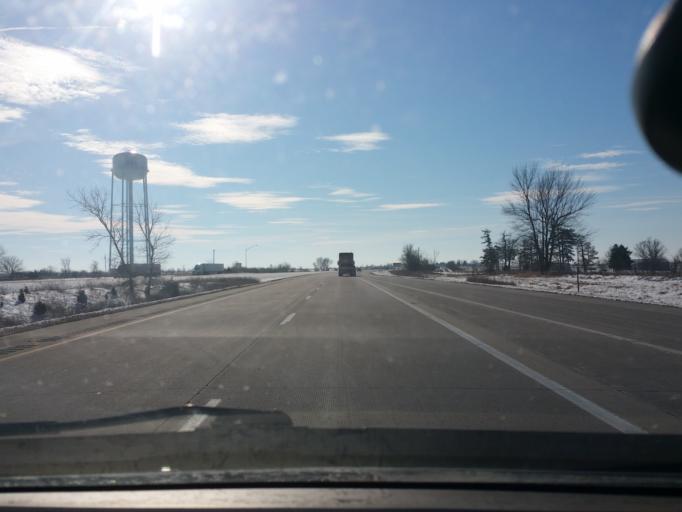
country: US
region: Iowa
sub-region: Clarke County
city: Osceola
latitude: 40.9895
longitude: -93.7983
